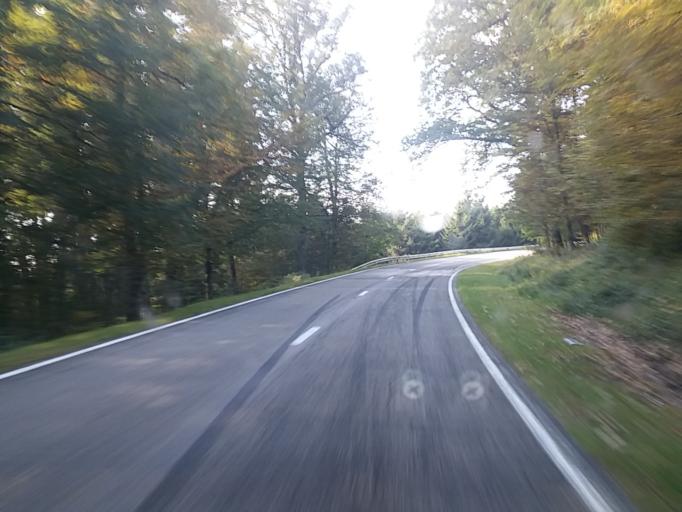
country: BE
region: Wallonia
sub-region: Province du Luxembourg
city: Herbeumont
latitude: 49.7480
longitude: 5.2434
